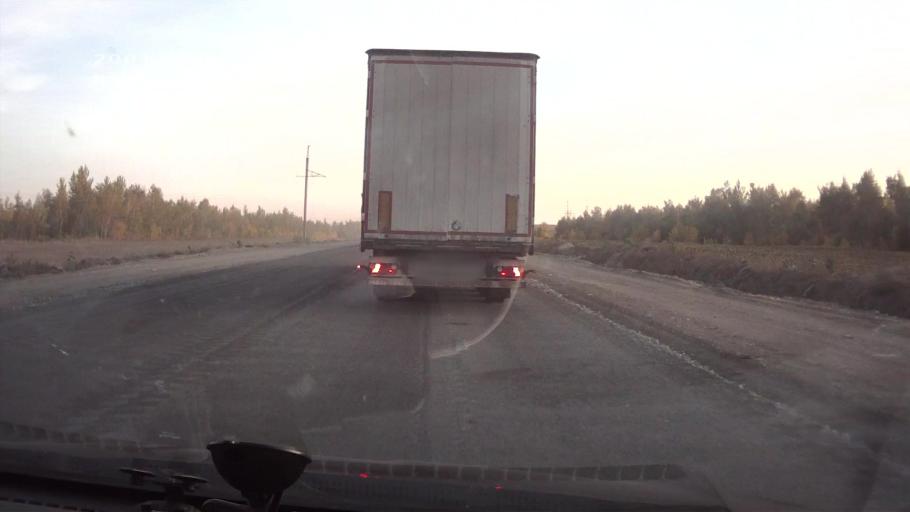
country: RU
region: Saratov
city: Kamenskiy
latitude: 50.9237
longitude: 45.5987
